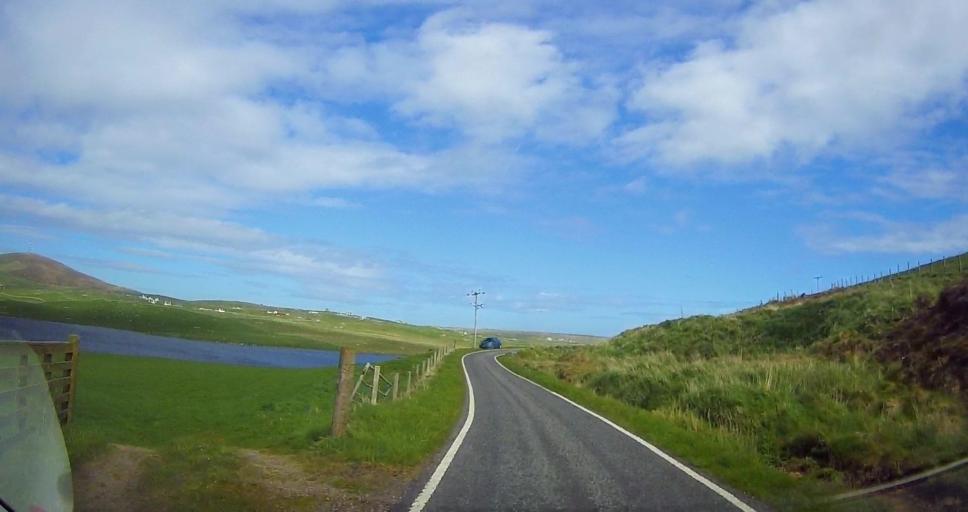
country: GB
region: Scotland
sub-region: Shetland Islands
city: Sandwick
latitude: 59.9244
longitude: -1.3380
